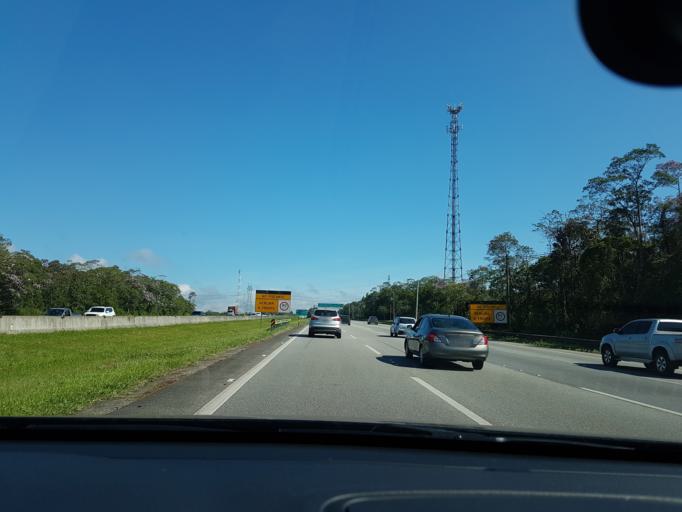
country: BR
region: Sao Paulo
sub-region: Cubatao
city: Cubatao
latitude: -23.8839
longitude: -46.5674
